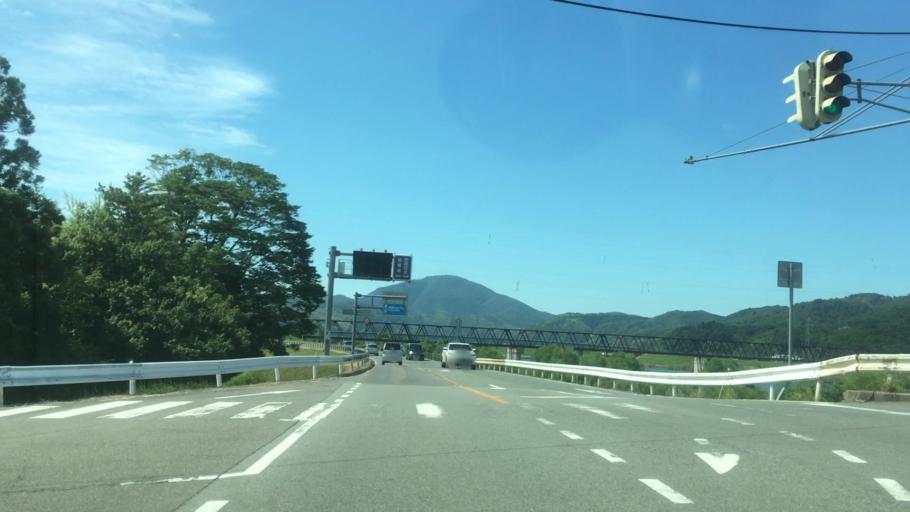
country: JP
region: Hyogo
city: Toyooka
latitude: 35.5503
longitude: 134.8247
